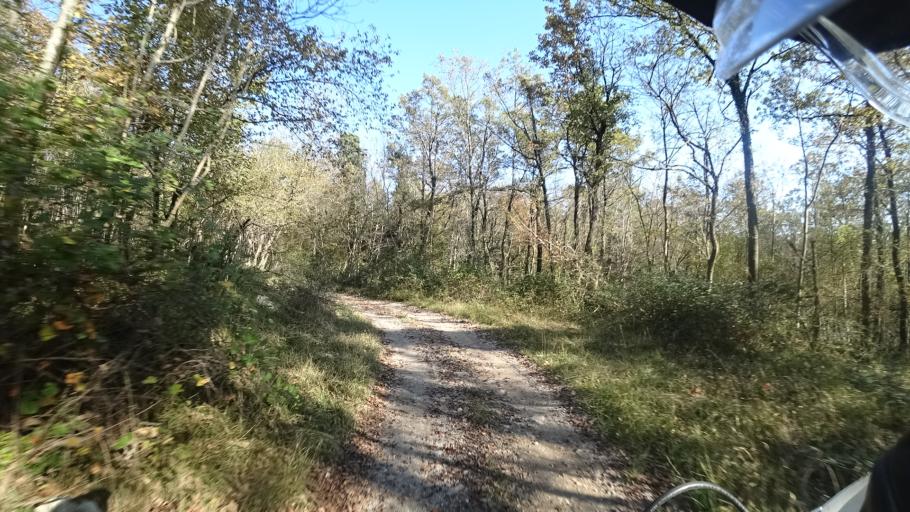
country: HR
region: Primorsko-Goranska
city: Kastav
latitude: 45.4024
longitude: 14.3304
